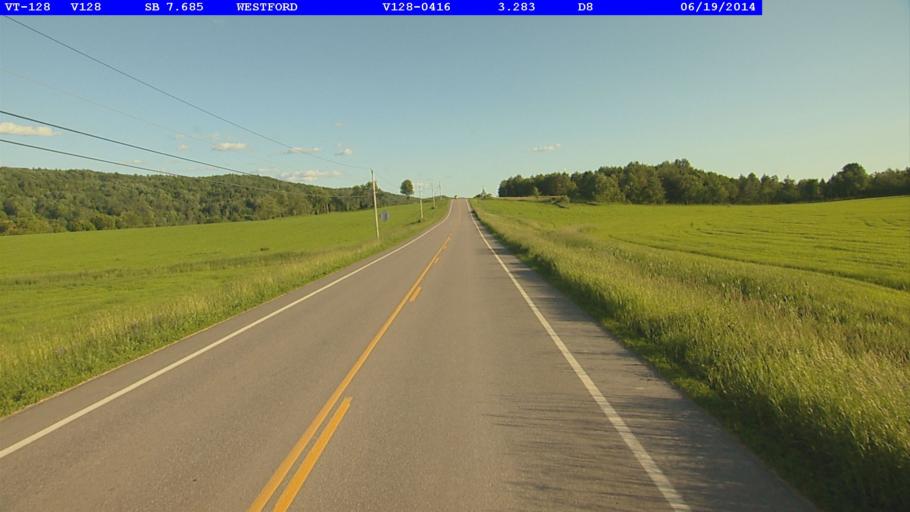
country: US
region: Vermont
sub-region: Chittenden County
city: Jericho
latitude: 44.6043
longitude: -73.0089
